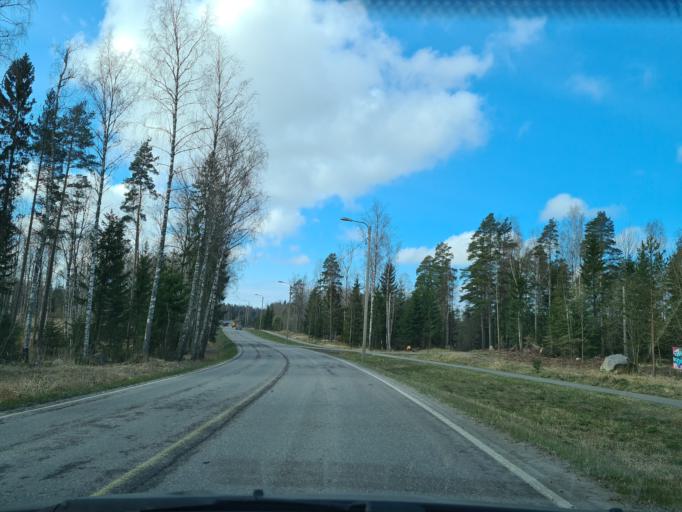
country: FI
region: Uusimaa
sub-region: Helsinki
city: Kirkkonummi
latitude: 60.0825
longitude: 24.4021
